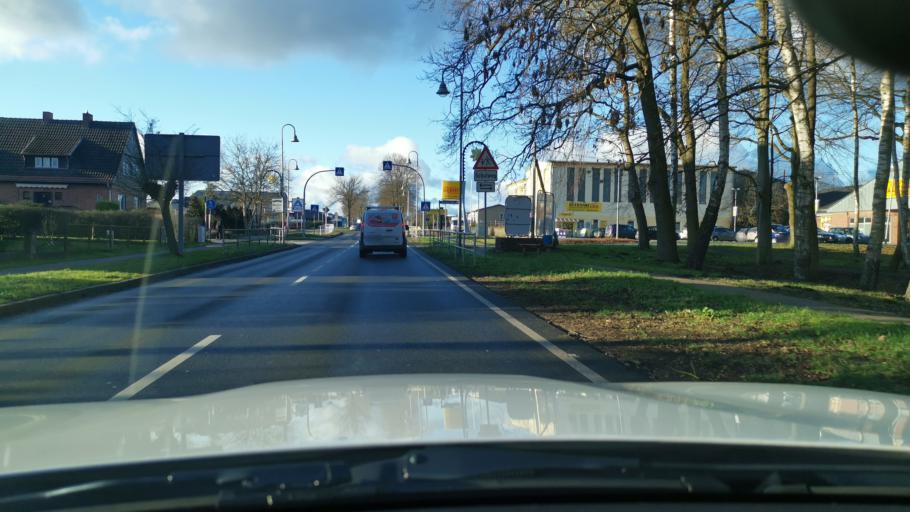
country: DE
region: Mecklenburg-Vorpommern
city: Tessin
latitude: 54.0291
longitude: 12.4597
